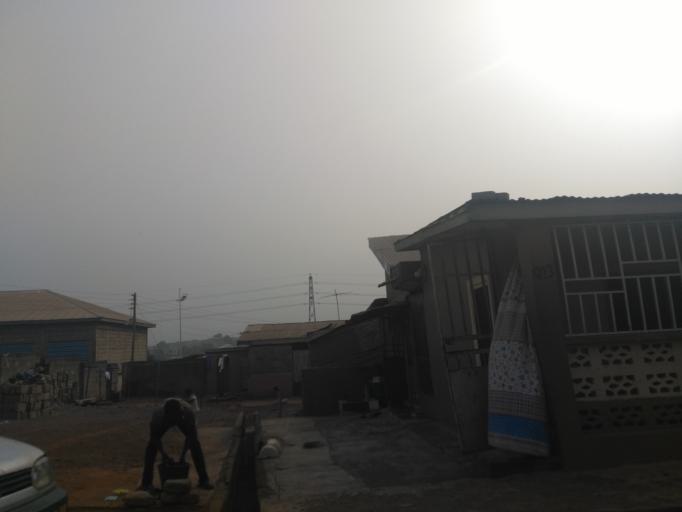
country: GH
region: Ashanti
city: Kumasi
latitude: 6.6990
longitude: -1.6410
